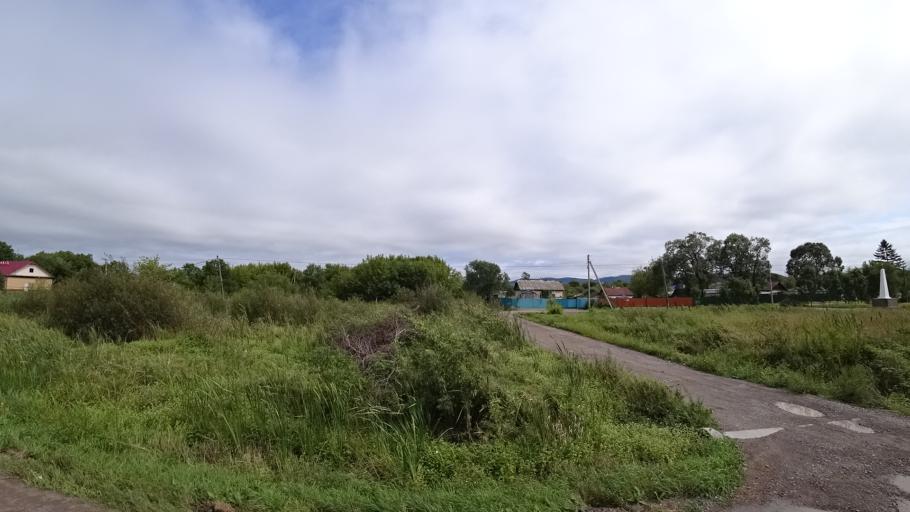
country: RU
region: Primorskiy
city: Monastyrishche
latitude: 44.1935
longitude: 132.4803
